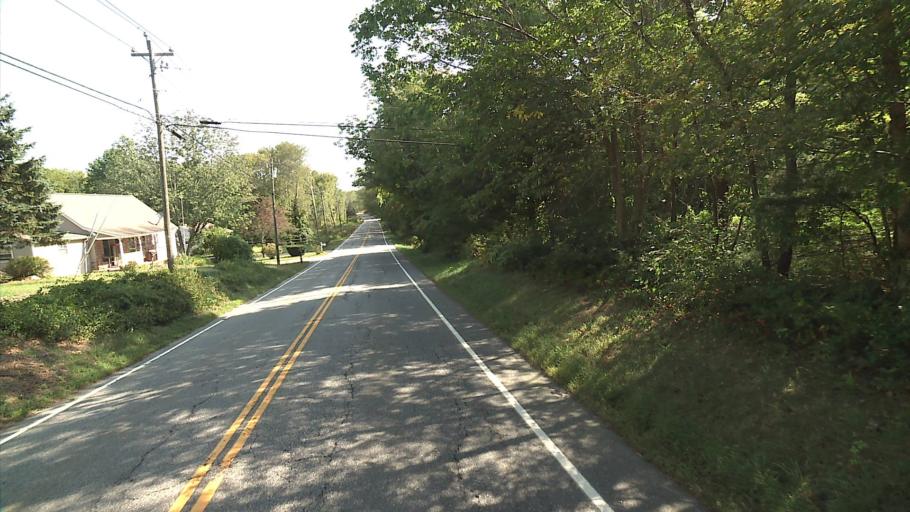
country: US
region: Connecticut
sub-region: New London County
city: Lisbon
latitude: 41.6298
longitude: -72.0041
